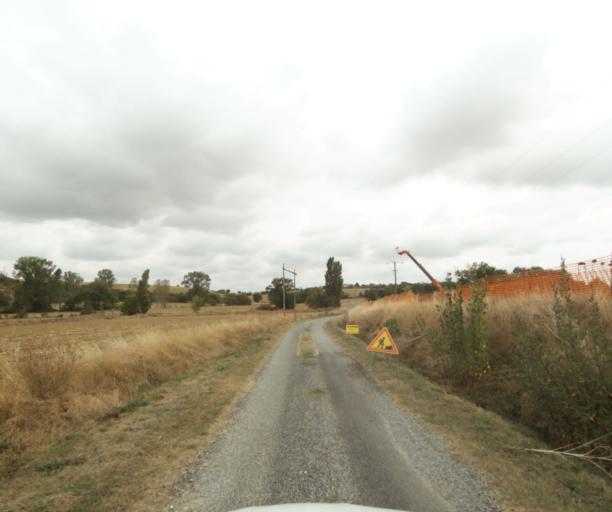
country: FR
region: Midi-Pyrenees
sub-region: Departement de la Haute-Garonne
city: Villefranche-de-Lauragais
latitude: 43.4161
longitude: 1.7305
